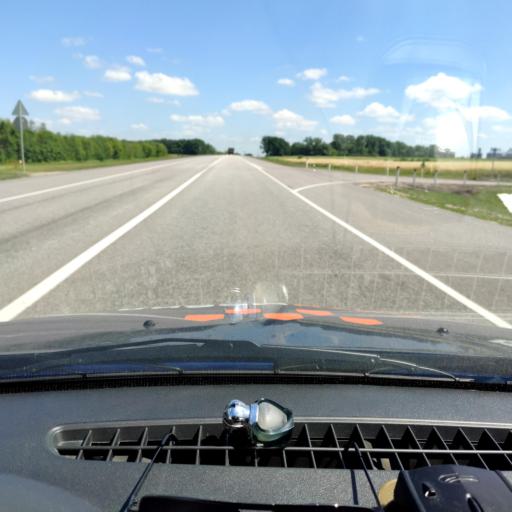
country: RU
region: Orjol
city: Orel
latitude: 52.8518
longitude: 36.2353
